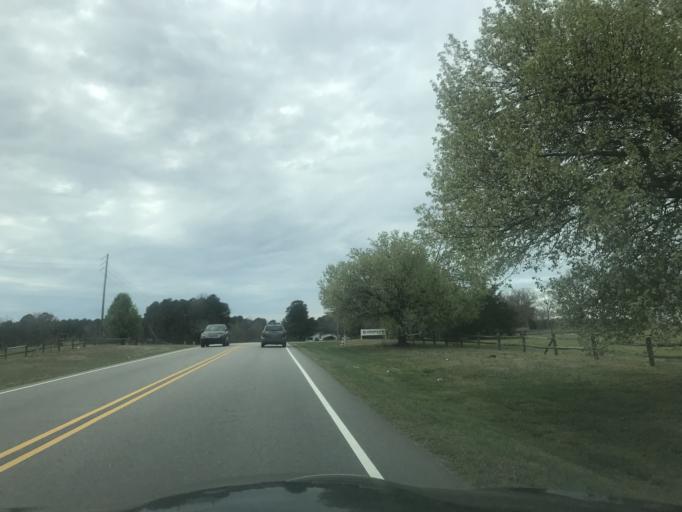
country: US
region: North Carolina
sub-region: Franklin County
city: Franklinton
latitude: 36.0953
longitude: -78.4163
